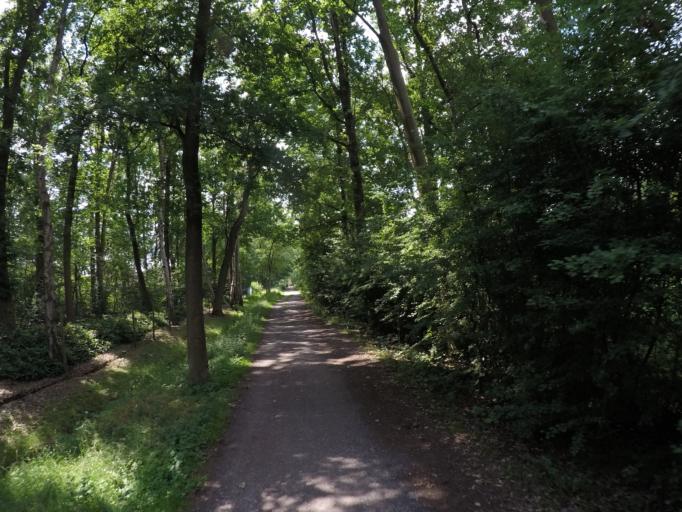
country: BE
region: Flanders
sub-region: Provincie Antwerpen
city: Schilde
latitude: 51.2675
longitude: 4.6013
